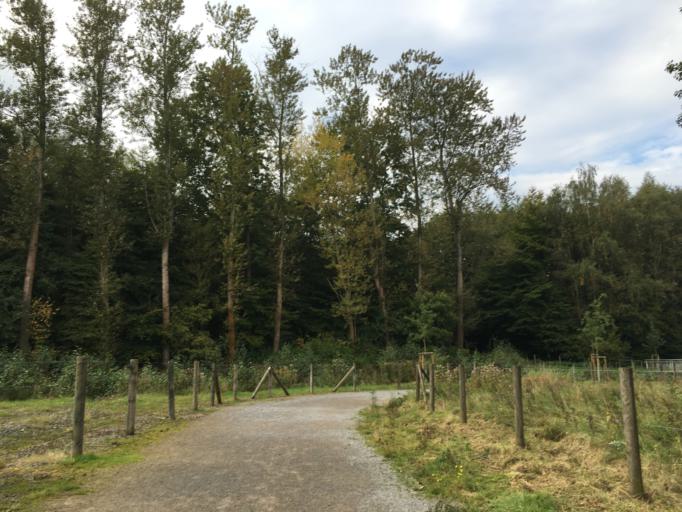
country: DE
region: North Rhine-Westphalia
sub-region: Regierungsbezirk Arnsberg
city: Dortmund
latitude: 51.4786
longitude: 7.4269
